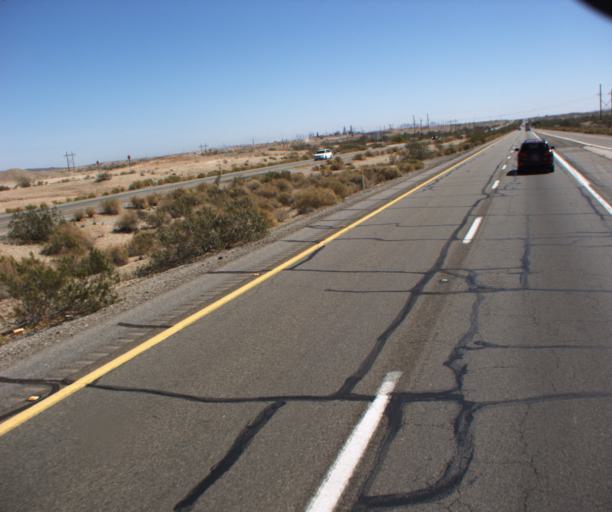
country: US
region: Arizona
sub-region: Yuma County
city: Fortuna Foothills
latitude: 32.6663
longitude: -114.2813
